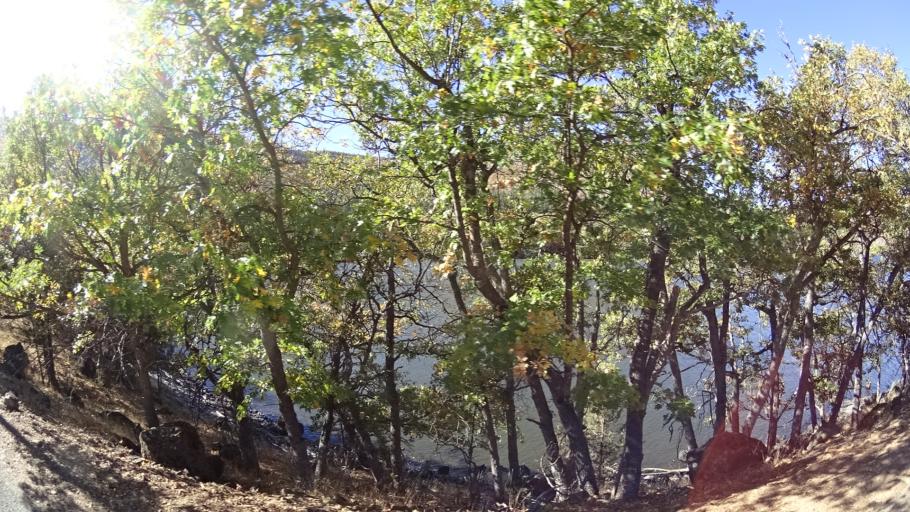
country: US
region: California
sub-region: Siskiyou County
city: Montague
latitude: 41.9679
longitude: -122.2706
